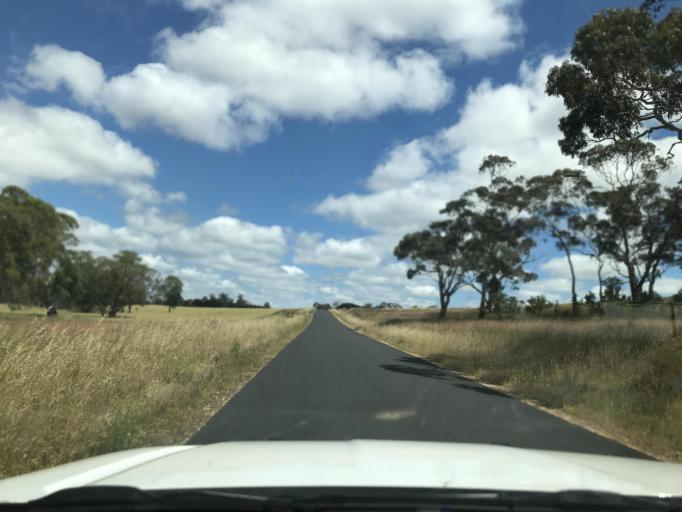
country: AU
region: South Australia
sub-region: Naracoorte and Lucindale
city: Naracoorte
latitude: -36.6706
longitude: 141.2895
